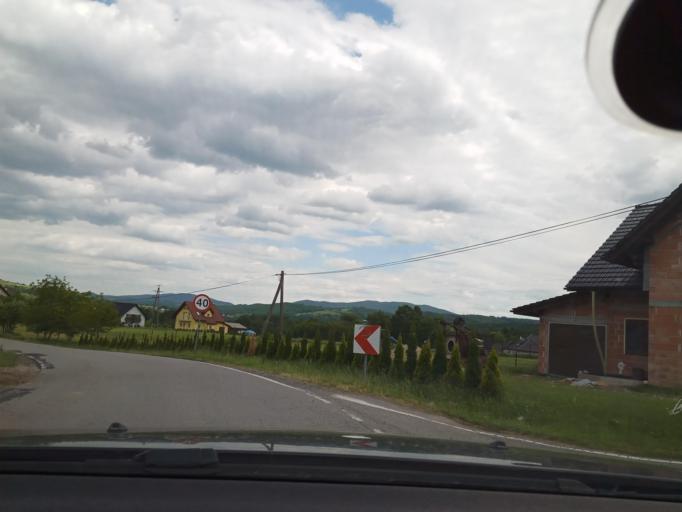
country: PL
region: Lesser Poland Voivodeship
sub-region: Powiat bochenski
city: Lapanow
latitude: 49.8370
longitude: 20.2750
